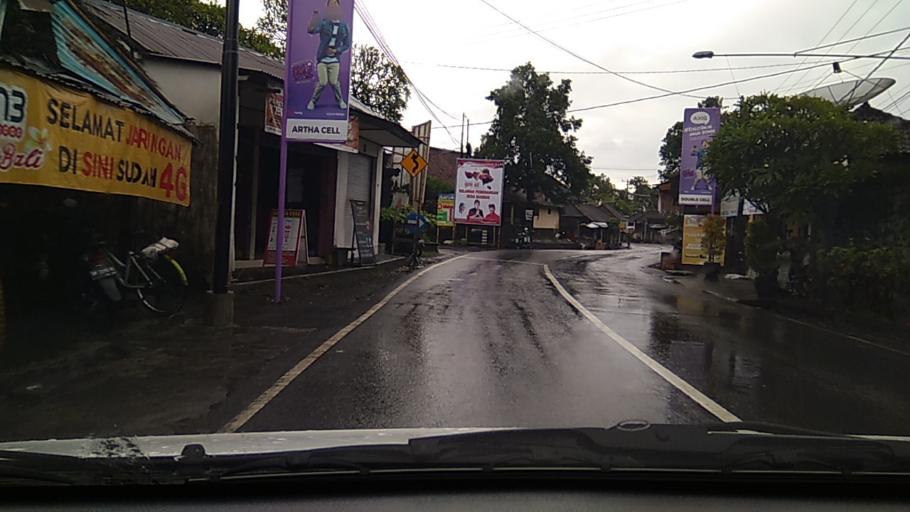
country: ID
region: Bali
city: Banjar Bugbug
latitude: -8.4909
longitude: 115.5942
